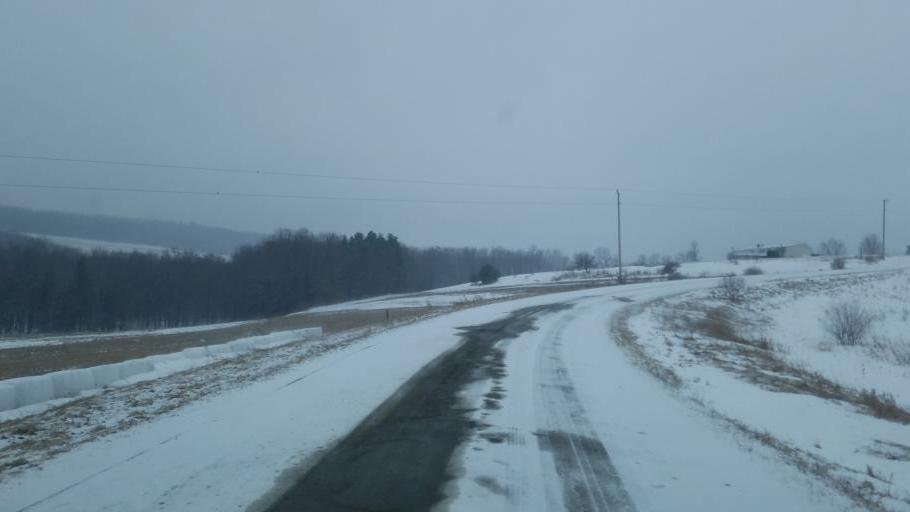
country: US
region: New York
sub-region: Steuben County
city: Canisteo
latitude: 42.1296
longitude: -77.5145
